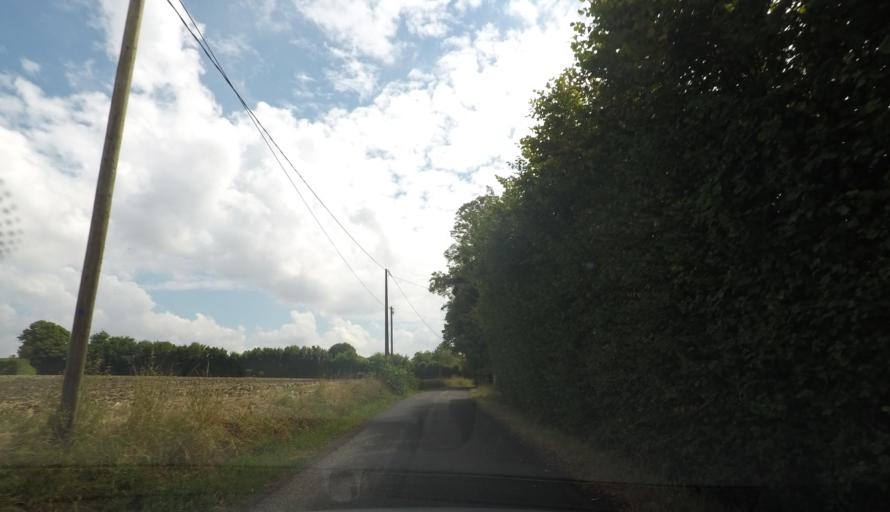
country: FR
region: Pays de la Loire
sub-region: Departement de la Sarthe
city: La Ferte-Bernard
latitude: 48.2663
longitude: 0.5954
